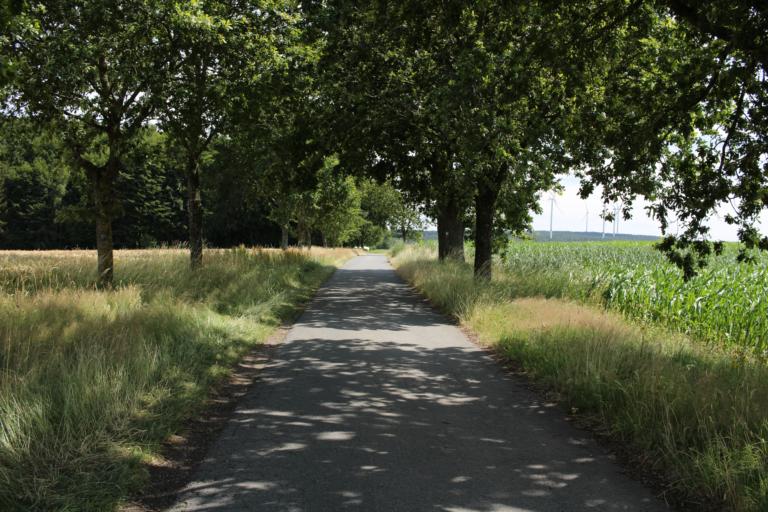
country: DE
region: Hesse
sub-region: Regierungsbezirk Darmstadt
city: Erbach
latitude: 49.6634
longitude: 8.9407
